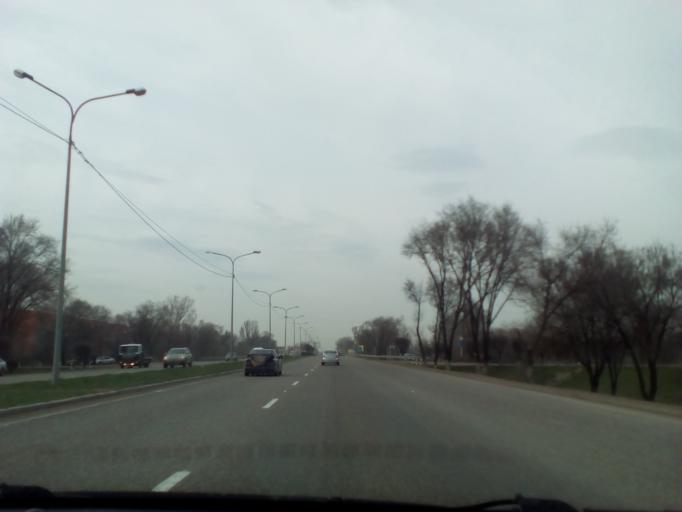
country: KZ
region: Almaty Oblysy
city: Burunday
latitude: 43.2184
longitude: 76.6469
